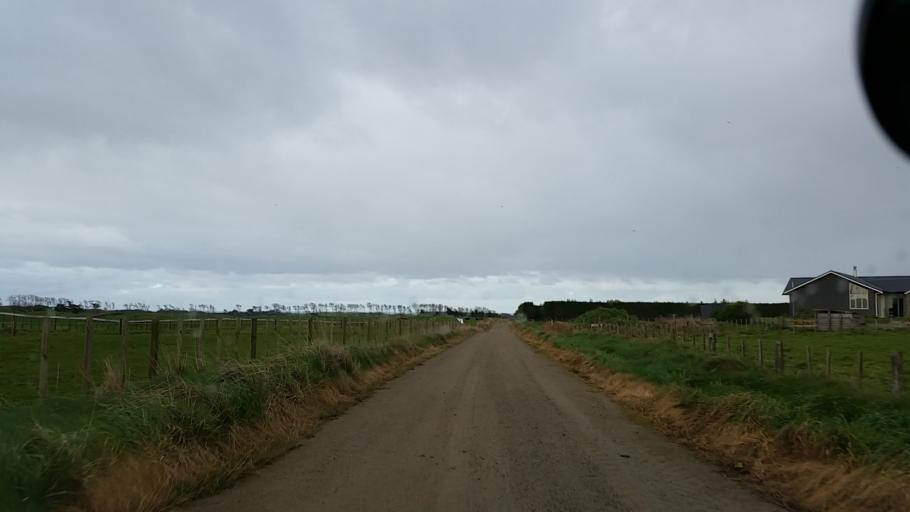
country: NZ
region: Taranaki
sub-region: South Taranaki District
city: Patea
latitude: -39.7636
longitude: 174.6426
